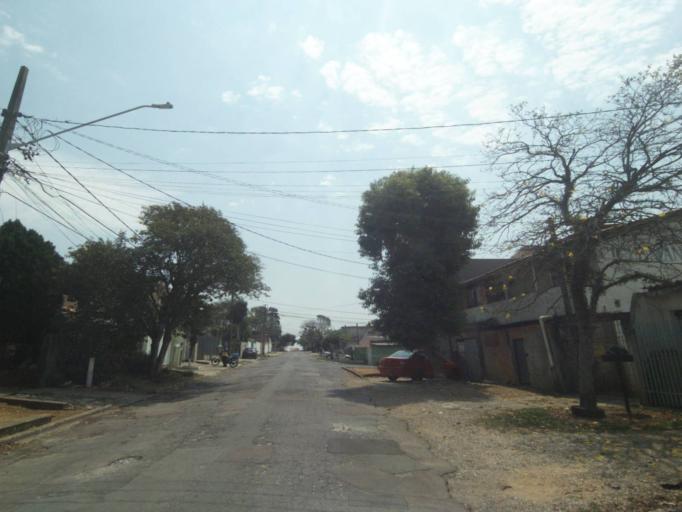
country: BR
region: Parana
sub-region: Sao Jose Dos Pinhais
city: Sao Jose dos Pinhais
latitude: -25.5337
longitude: -49.2450
